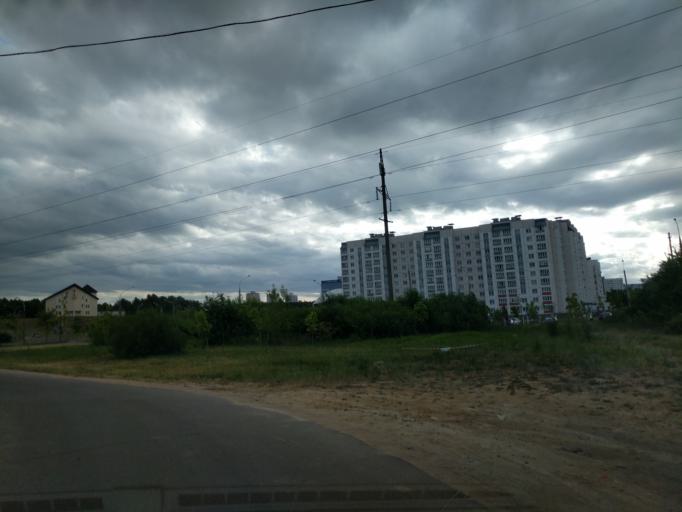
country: BY
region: Minsk
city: Novoye Medvezhino
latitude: 53.8947
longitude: 27.4648
